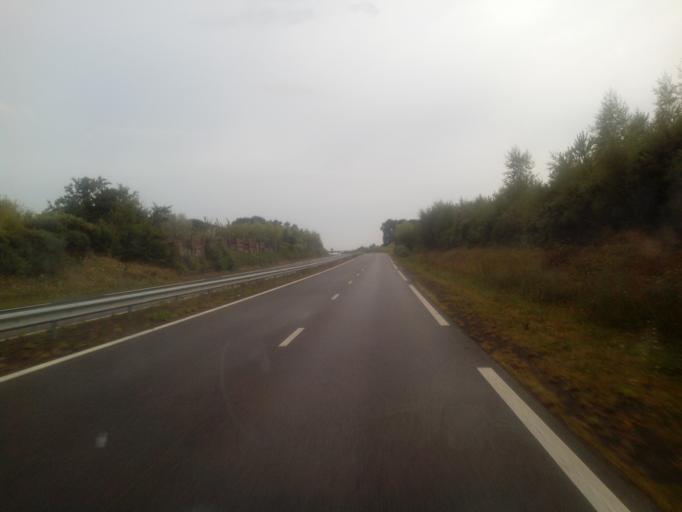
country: FR
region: Brittany
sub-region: Departement d'Ille-et-Vilaine
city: Betton
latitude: 48.1867
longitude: -1.6240
